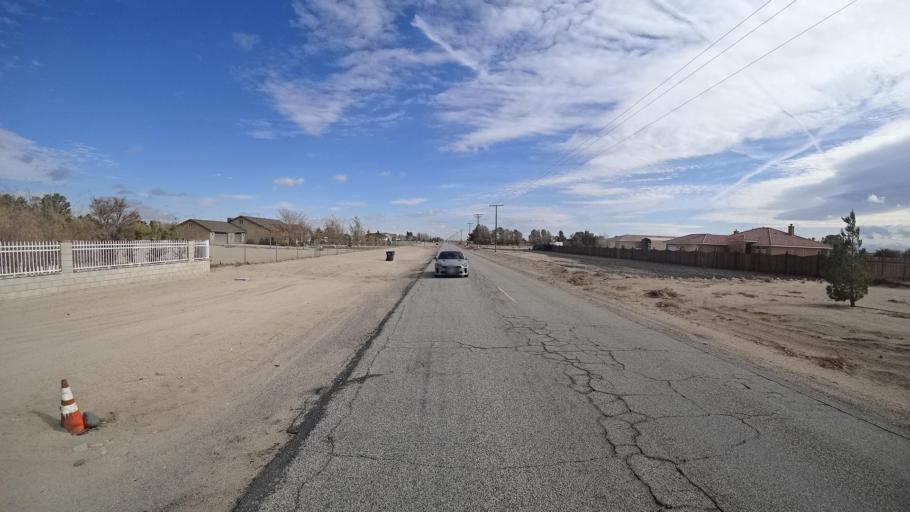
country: US
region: California
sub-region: Kern County
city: Rosamond
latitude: 34.8203
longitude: -118.2630
